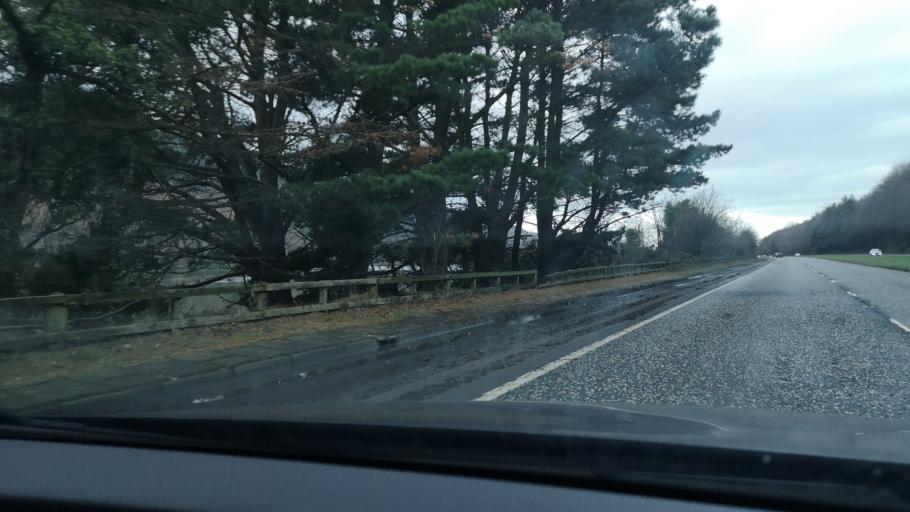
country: GB
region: Northern Ireland
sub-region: Down District
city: Warrenpoint
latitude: 54.1190
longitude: -6.2953
